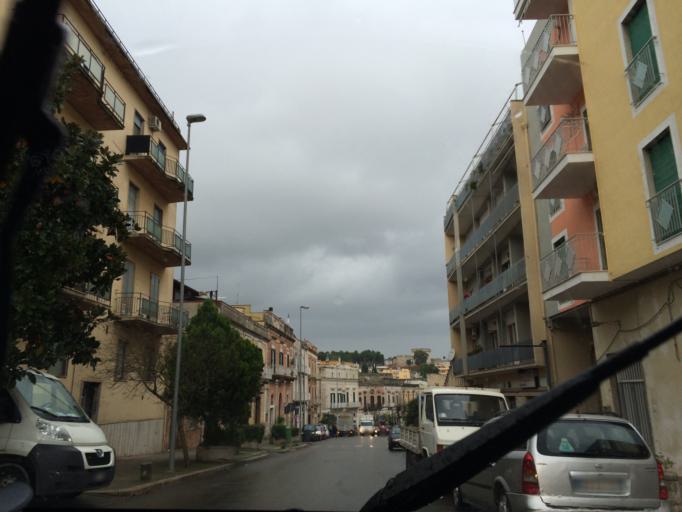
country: IT
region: Basilicate
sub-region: Provincia di Matera
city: Matera
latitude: 40.6608
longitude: 16.6116
